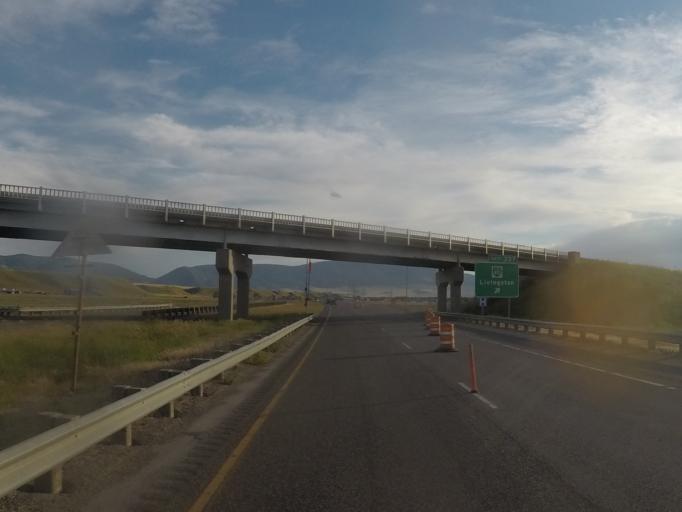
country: US
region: Montana
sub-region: Park County
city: Livingston
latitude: 45.6884
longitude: -110.4999
